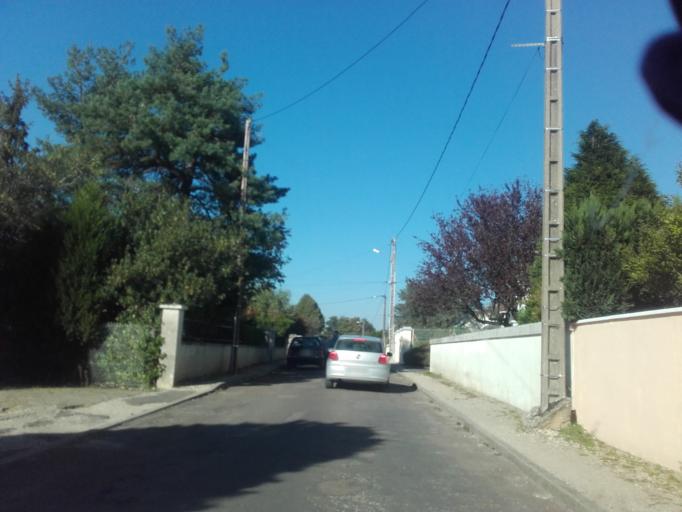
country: FR
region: Bourgogne
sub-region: Departement de Saone-et-Loire
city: Chagny
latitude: 46.9099
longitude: 4.7575
